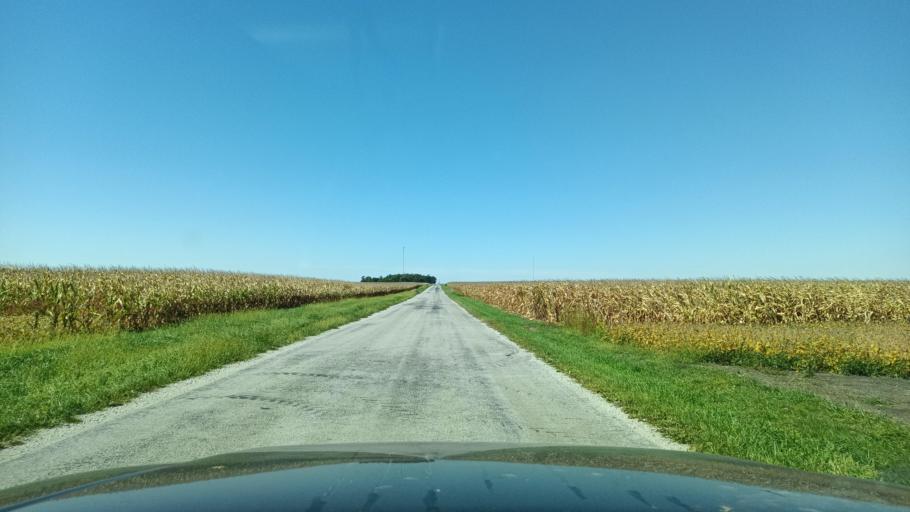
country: US
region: Illinois
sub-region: Champaign County
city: Mahomet
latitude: 40.0989
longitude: -88.3832
